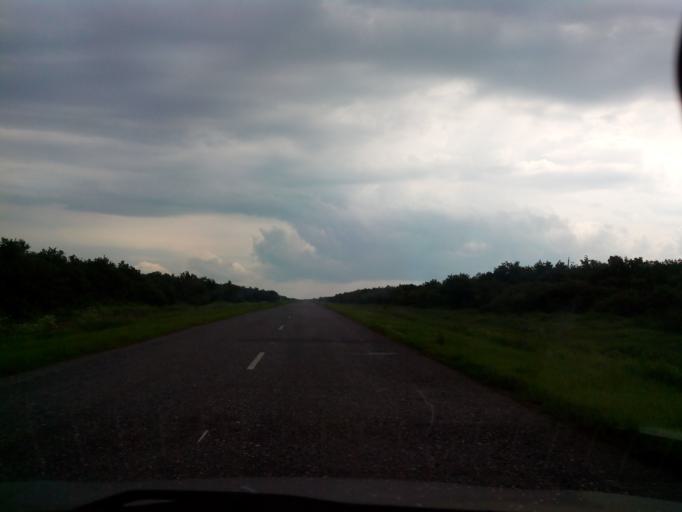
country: RU
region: Volgograd
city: Kumylzhenskaya
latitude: 49.8915
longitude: 42.8092
